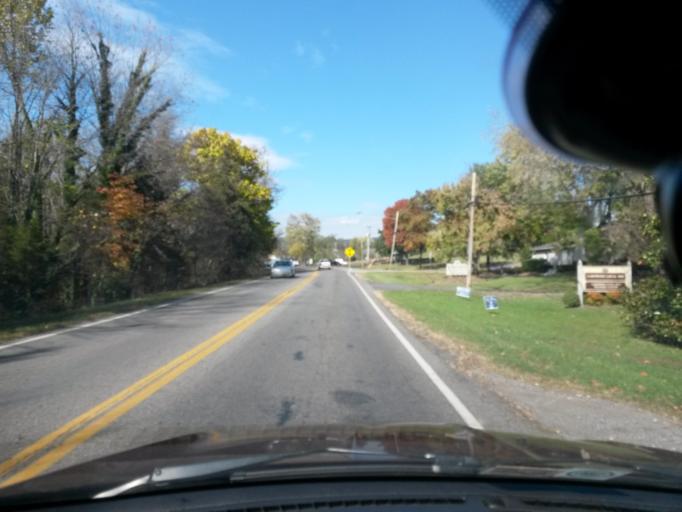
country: US
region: Virginia
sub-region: Roanoke County
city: Hollins
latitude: 37.3386
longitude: -79.9694
